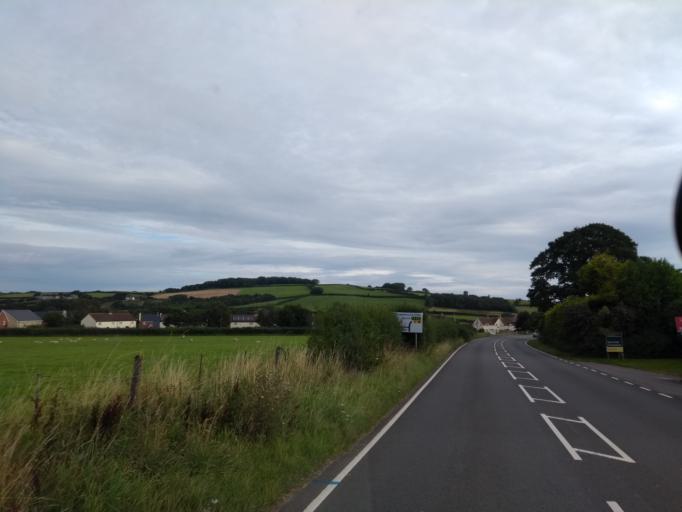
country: GB
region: England
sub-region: Somerset
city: Crewkerne
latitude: 50.8398
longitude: -2.7767
